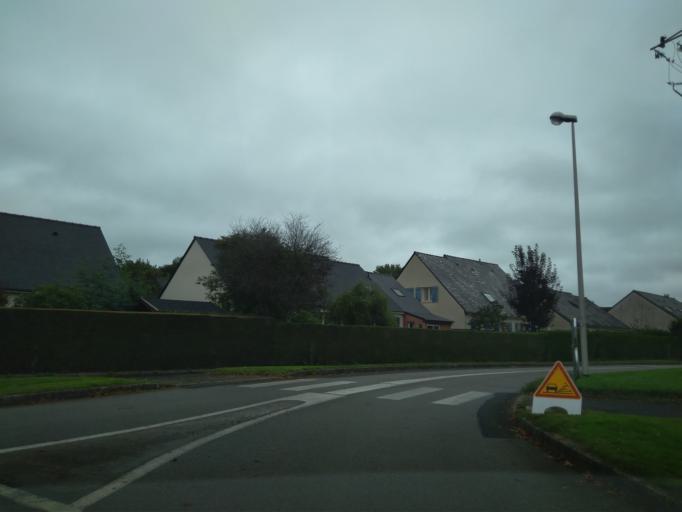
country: FR
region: Brittany
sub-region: Departement d'Ille-et-Vilaine
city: Betton
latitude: 48.1720
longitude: -1.6371
